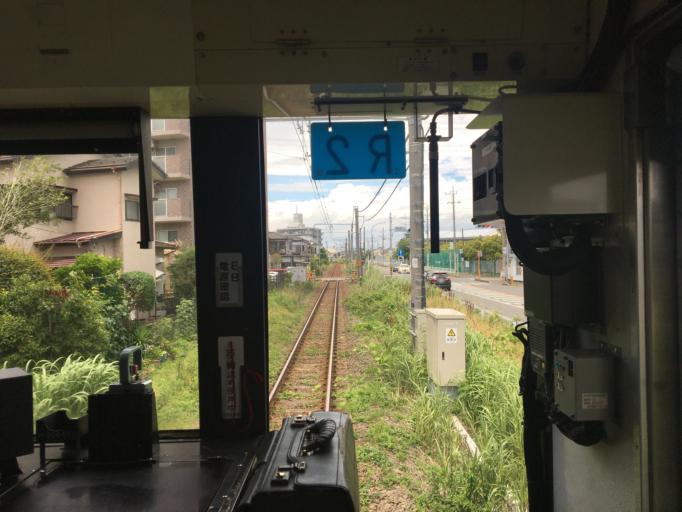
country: JP
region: Kanagawa
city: Atsugi
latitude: 35.4075
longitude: 139.3797
